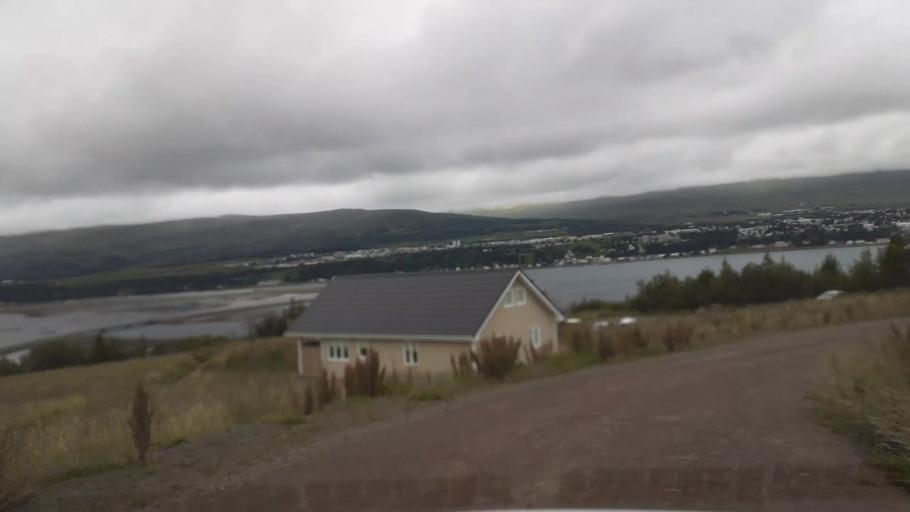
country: IS
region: Northeast
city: Akureyri
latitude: 65.6763
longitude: -18.0401
